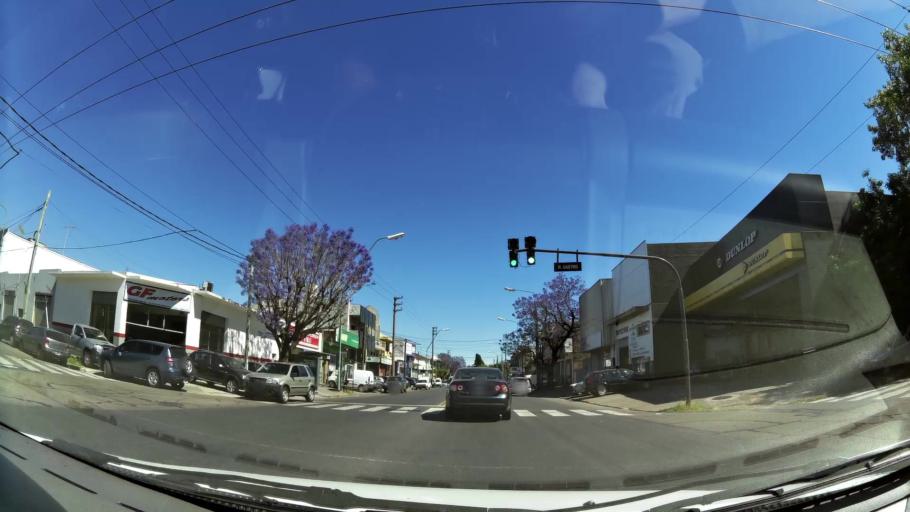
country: AR
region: Buenos Aires
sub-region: Partido de Vicente Lopez
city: Olivos
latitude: -34.5204
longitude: -58.5239
